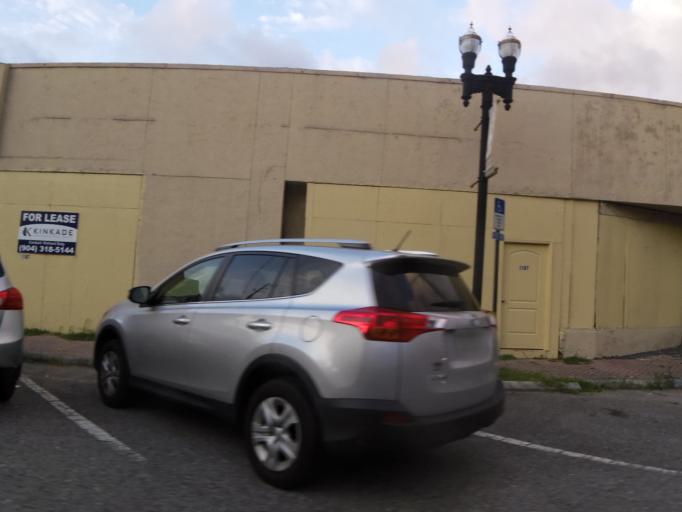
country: US
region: Florida
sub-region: Duval County
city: Jacksonville
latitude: 30.3084
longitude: -81.7136
